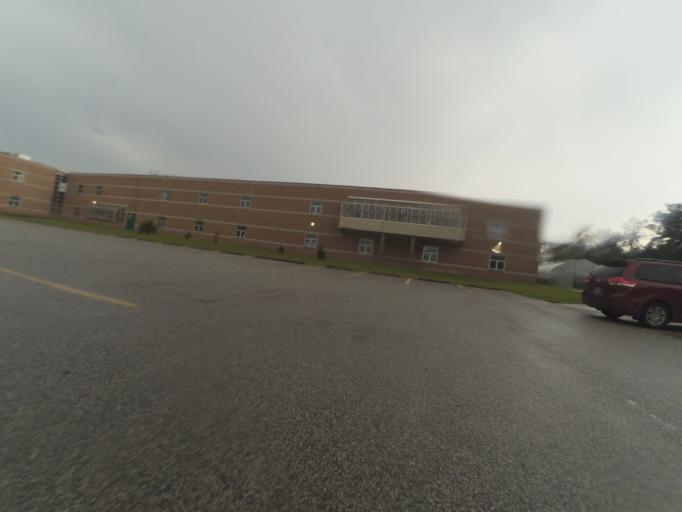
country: US
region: West Virginia
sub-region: Cabell County
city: Huntington
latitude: 38.3946
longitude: -82.4001
